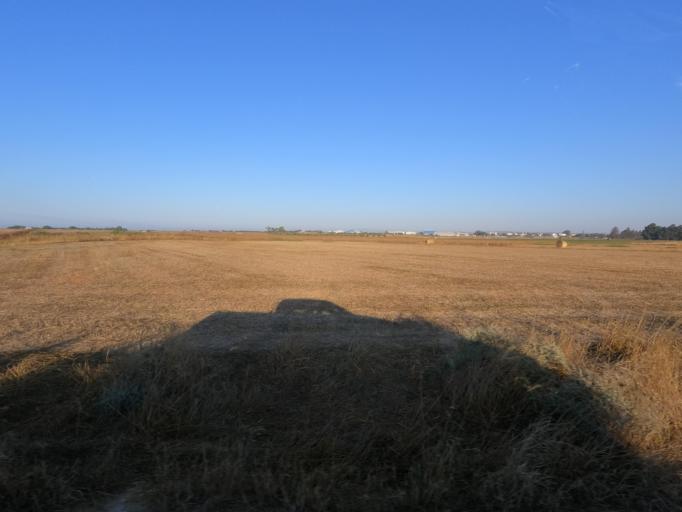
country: CY
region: Ammochostos
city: Achna
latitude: 35.0230
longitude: 33.7942
